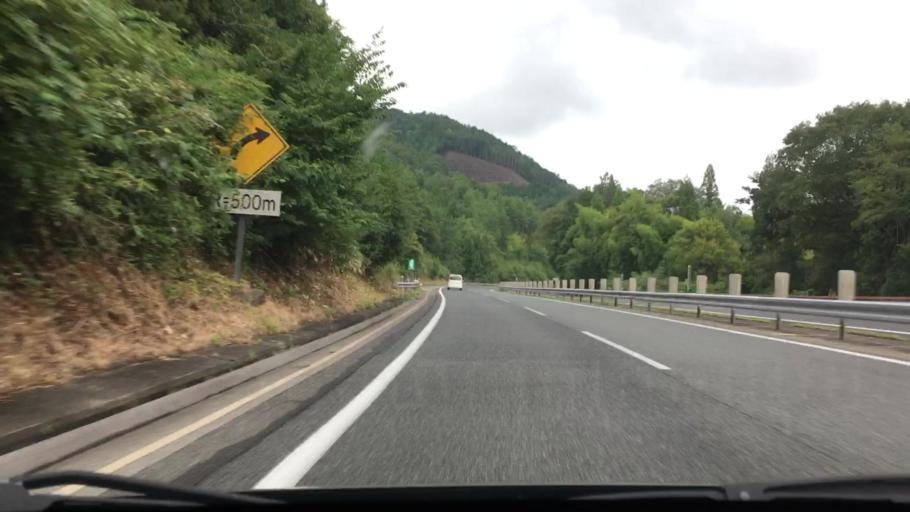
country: JP
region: Hiroshima
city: Miyoshi
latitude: 34.7055
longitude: 132.6133
